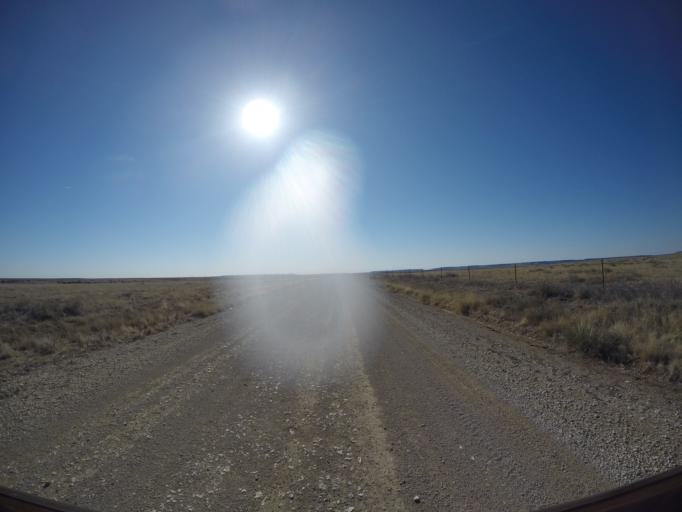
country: US
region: Colorado
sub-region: Otero County
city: La Junta
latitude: 37.6955
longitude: -103.6204
